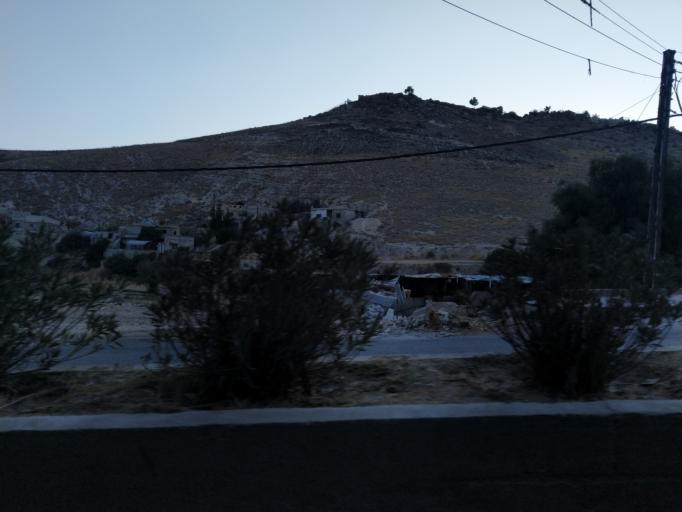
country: SY
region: Rif-dimashq
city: At Tall
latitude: 33.5733
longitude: 36.3049
